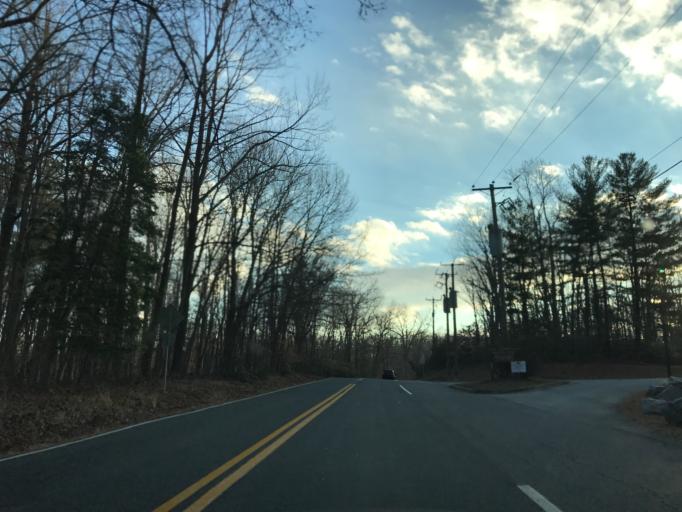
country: US
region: Maryland
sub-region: Cecil County
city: Charlestown
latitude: 39.4845
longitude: -75.9819
